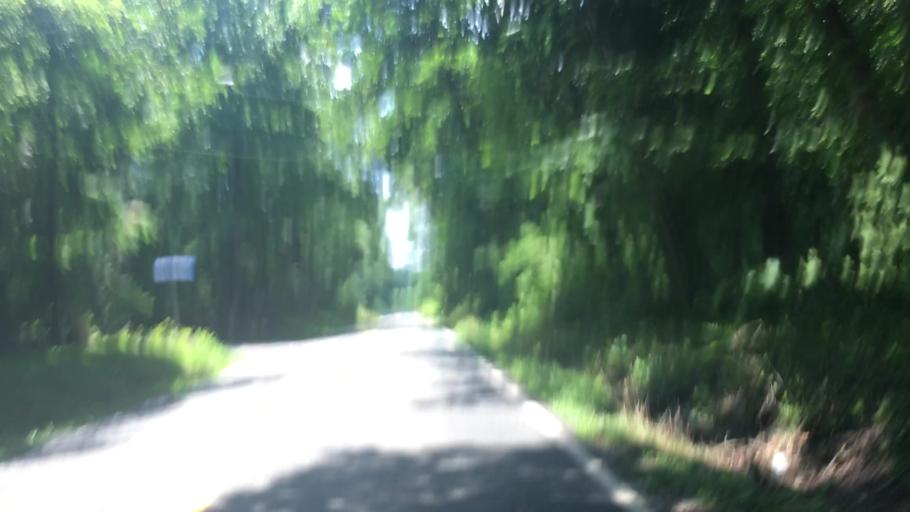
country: US
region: Virginia
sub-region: King George County
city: King George
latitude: 38.3346
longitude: -77.1391
